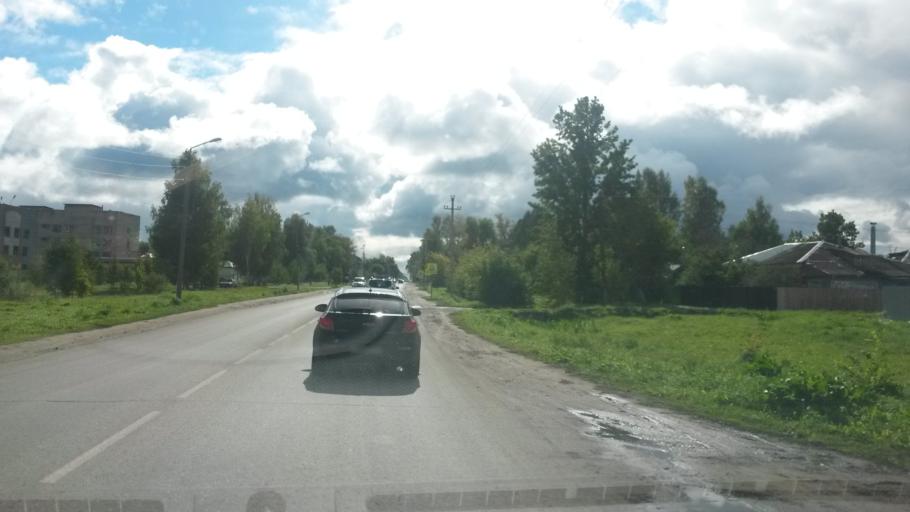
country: RU
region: Ivanovo
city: Zavolzhsk
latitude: 57.4965
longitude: 42.1324
